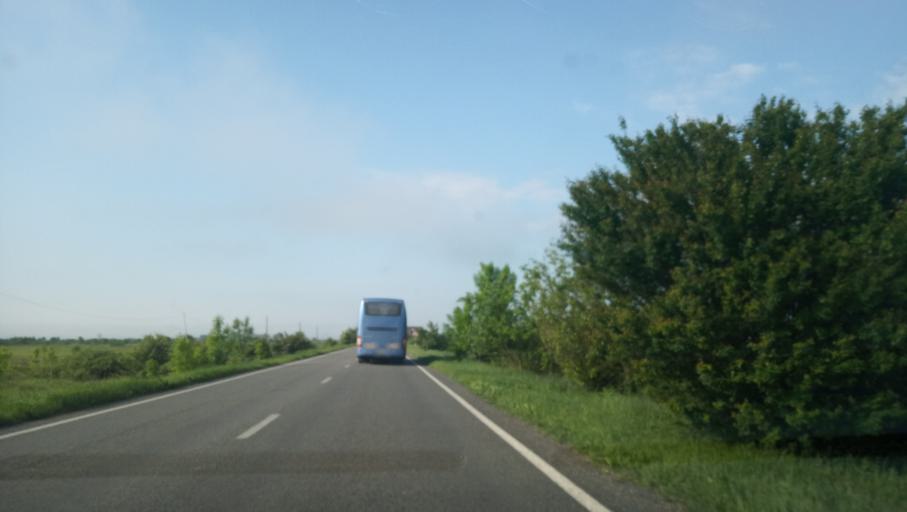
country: RO
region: Timis
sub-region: Comuna Moravita
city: Moravita
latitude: 45.2469
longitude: 21.2635
